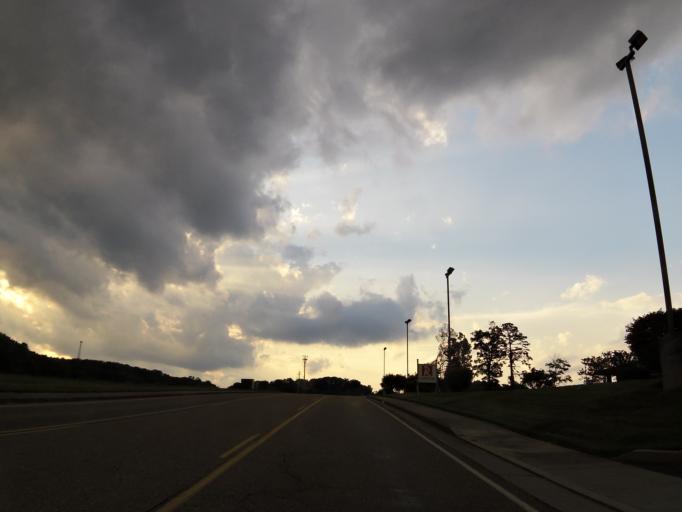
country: US
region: Tennessee
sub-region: Knox County
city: Knoxville
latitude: 36.0538
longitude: -84.0010
